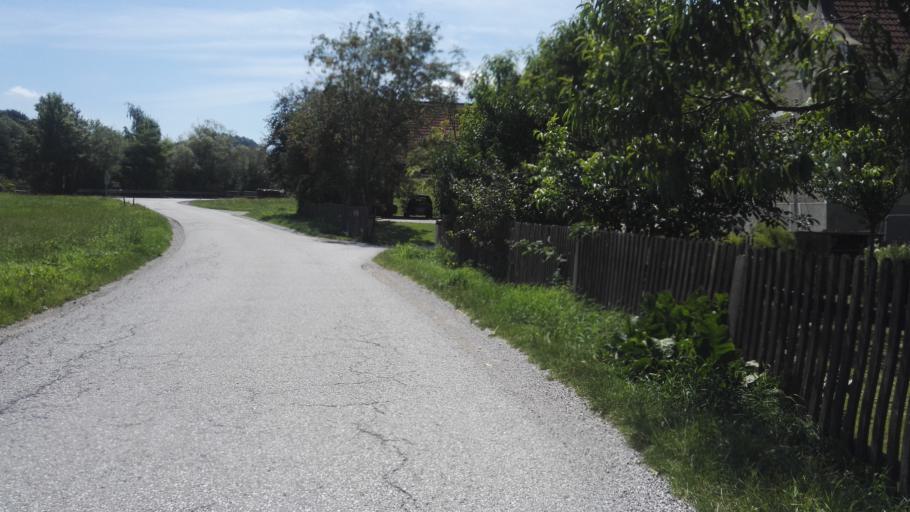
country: AT
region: Styria
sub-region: Politischer Bezirk Graz-Umgebung
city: Frohnleiten
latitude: 47.2647
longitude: 15.3144
